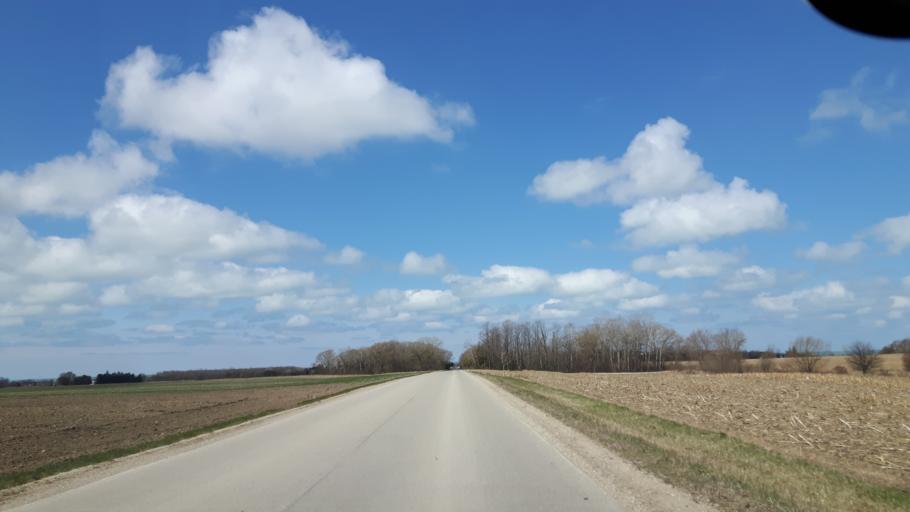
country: CA
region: Ontario
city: Goderich
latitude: 43.6985
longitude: -81.6914
